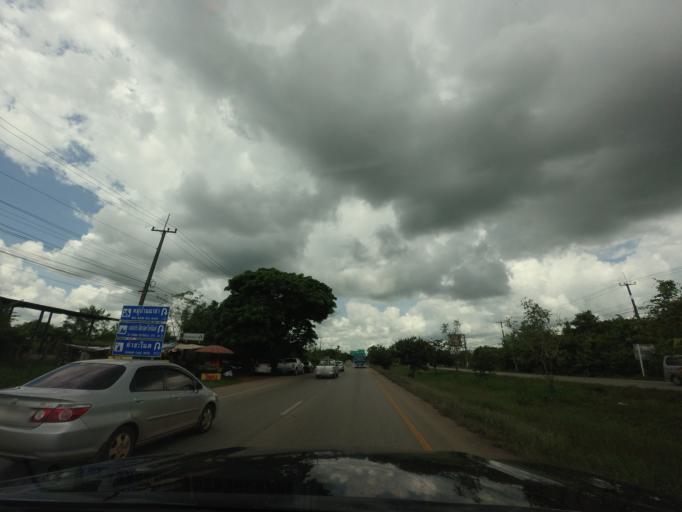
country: TH
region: Nong Khai
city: Sa Khrai
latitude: 17.5564
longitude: 102.8010
